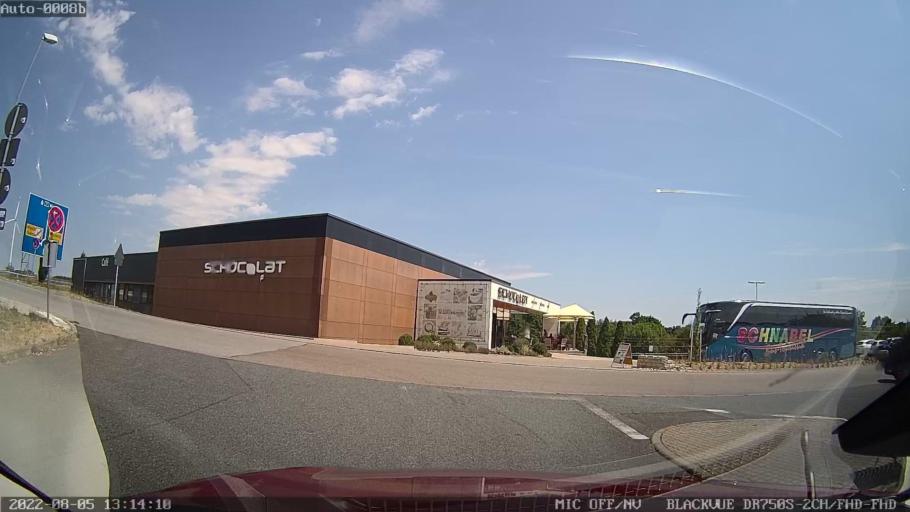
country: DE
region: Bavaria
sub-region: Upper Palatinate
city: Freystadt
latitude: 49.1722
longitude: 11.2726
